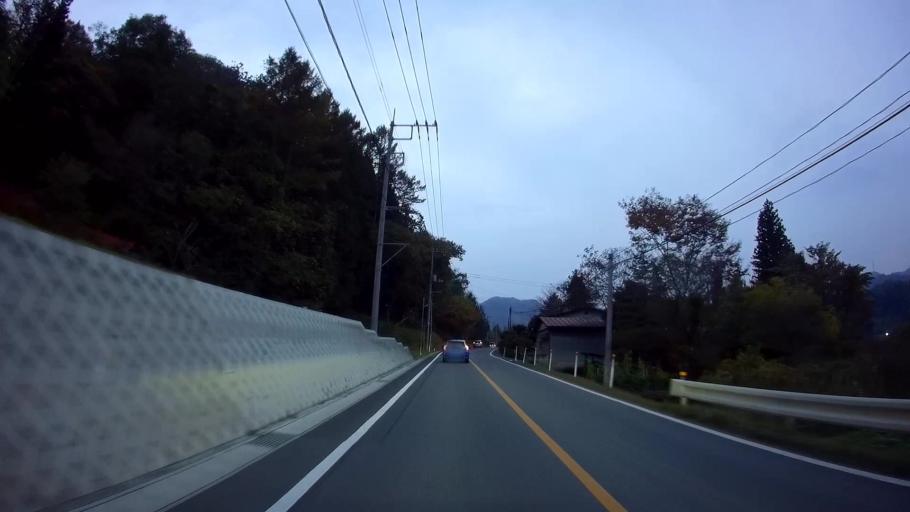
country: JP
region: Gunma
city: Nakanojomachi
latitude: 36.5396
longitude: 138.7902
